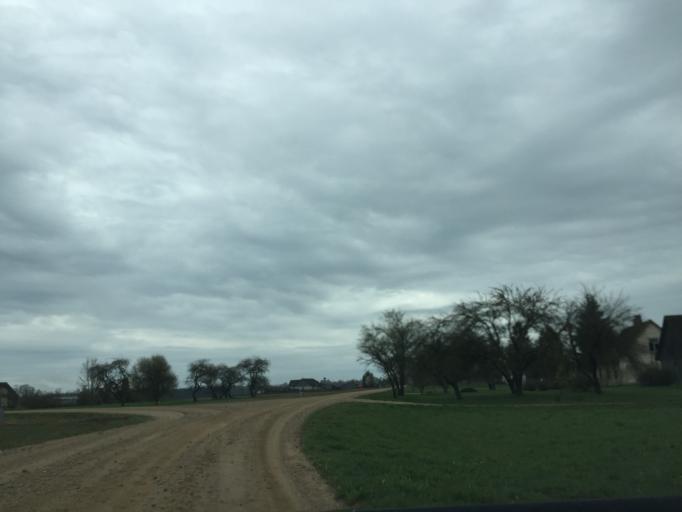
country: LV
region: Sigulda
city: Sigulda
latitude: 57.0422
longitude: 24.8441
